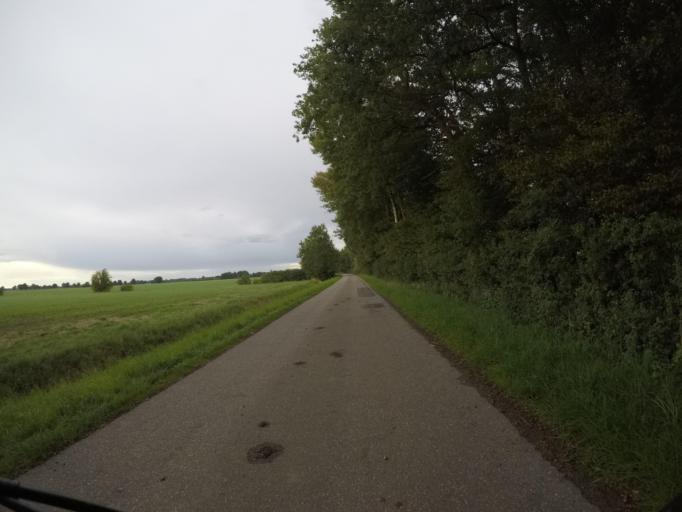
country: DE
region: Lower Saxony
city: Neu Darchau
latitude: 53.2743
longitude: 10.8814
